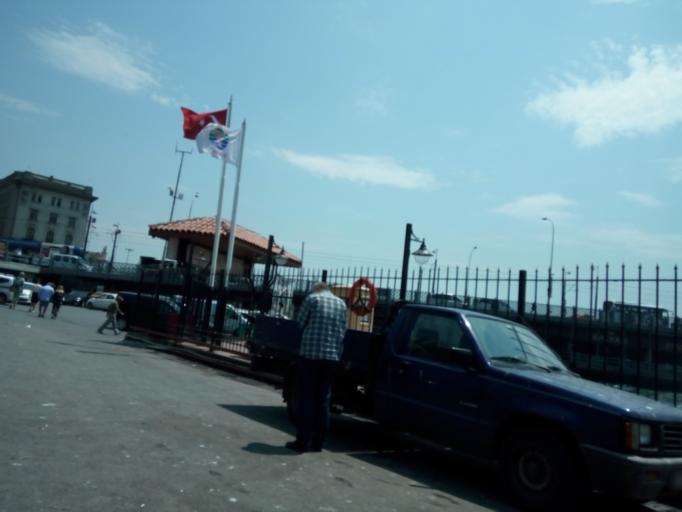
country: TR
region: Istanbul
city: Eminoenue
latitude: 41.0219
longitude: 28.9736
